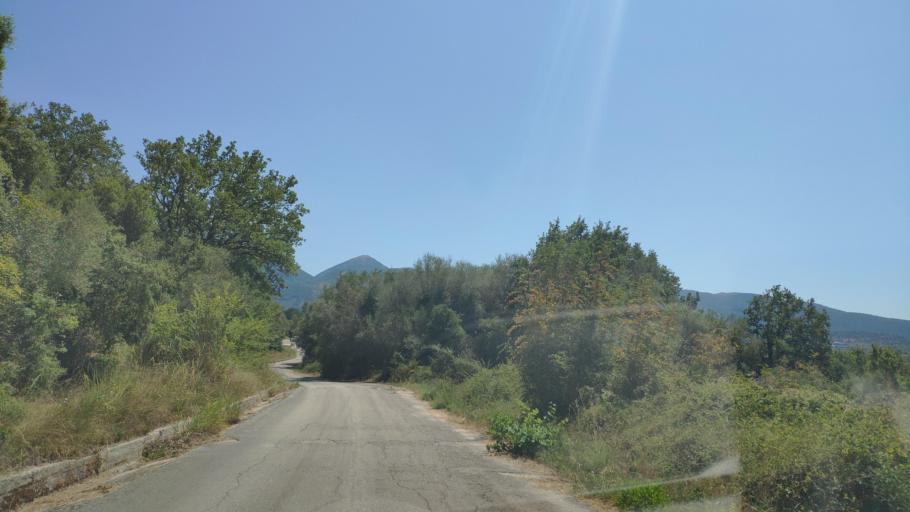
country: GR
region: Epirus
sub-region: Nomos Prevezis
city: Kanalaki
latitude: 39.2693
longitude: 20.6005
